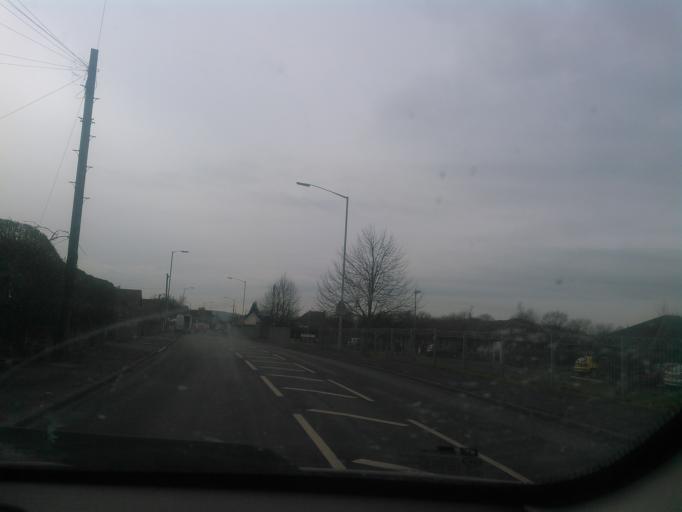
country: GB
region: England
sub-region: Telford and Wrekin
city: Oakengates
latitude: 52.7182
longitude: -2.4442
